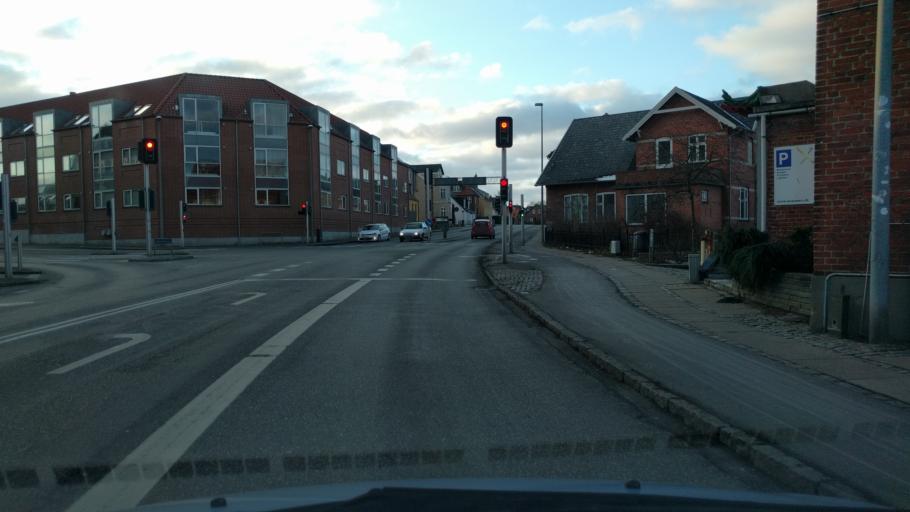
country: DK
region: Zealand
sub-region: Naestved Kommune
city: Naestved
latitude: 55.2301
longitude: 11.7530
